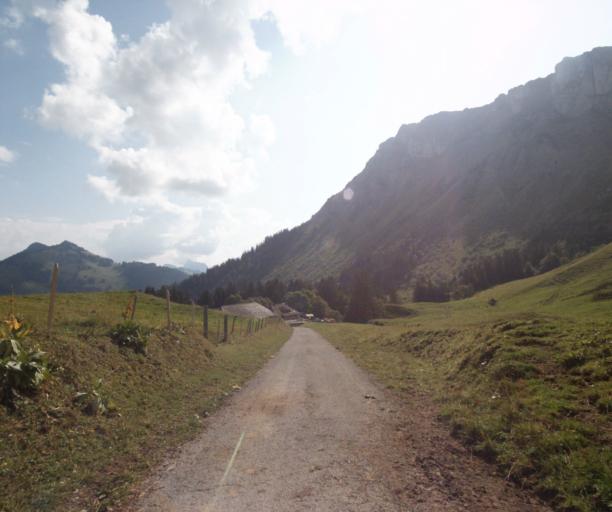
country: CH
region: Vaud
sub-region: Riviera-Pays-d'Enhaut District
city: Caux
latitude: 46.4275
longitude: 7.0008
